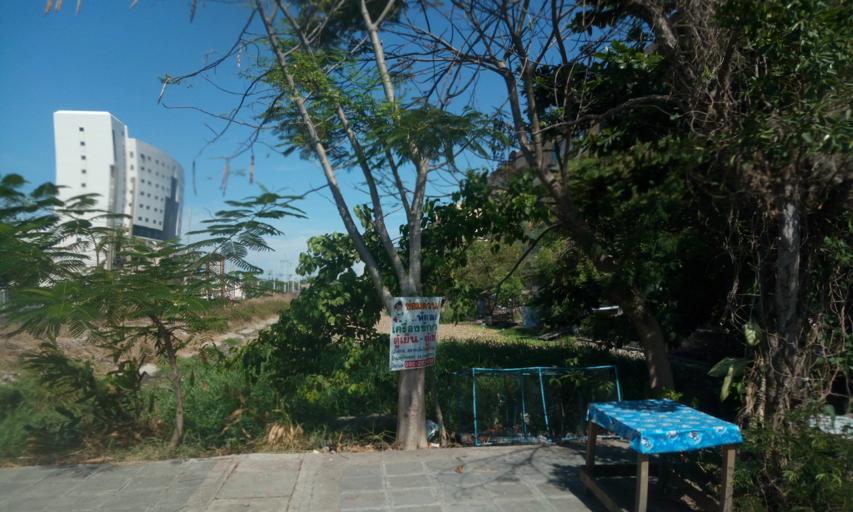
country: TH
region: Samut Prakan
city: Bang Bo District
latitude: 13.5629
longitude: 100.7663
